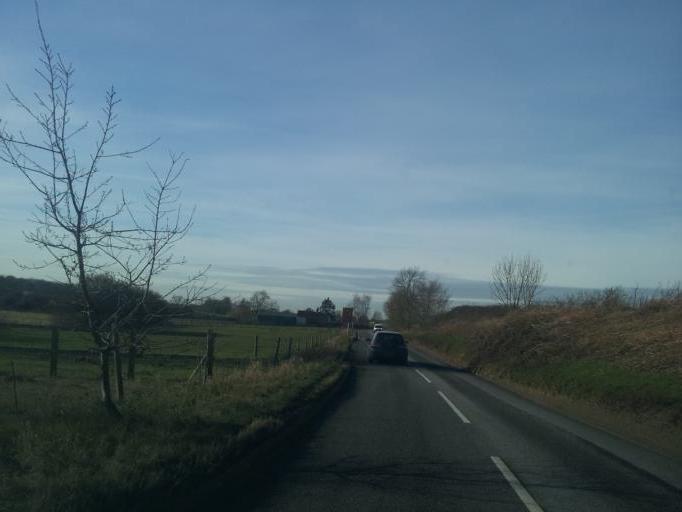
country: GB
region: England
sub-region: Suffolk
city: Wickham Market
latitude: 52.1606
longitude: 1.3263
